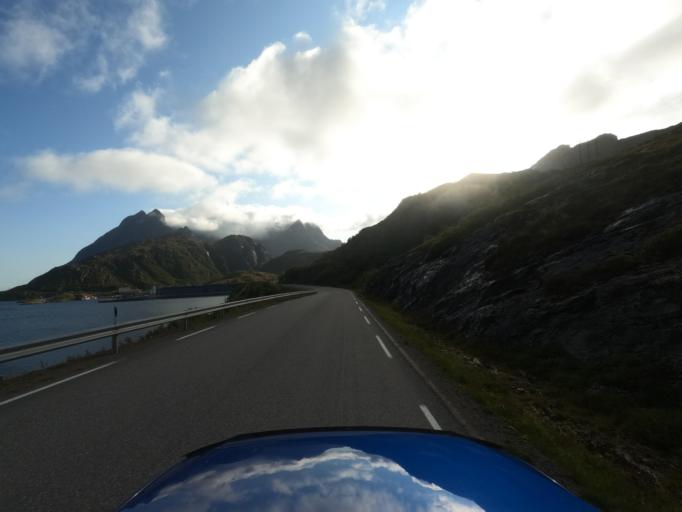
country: NO
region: Nordland
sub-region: Flakstad
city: Ramberg
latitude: 68.0140
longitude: 13.1716
